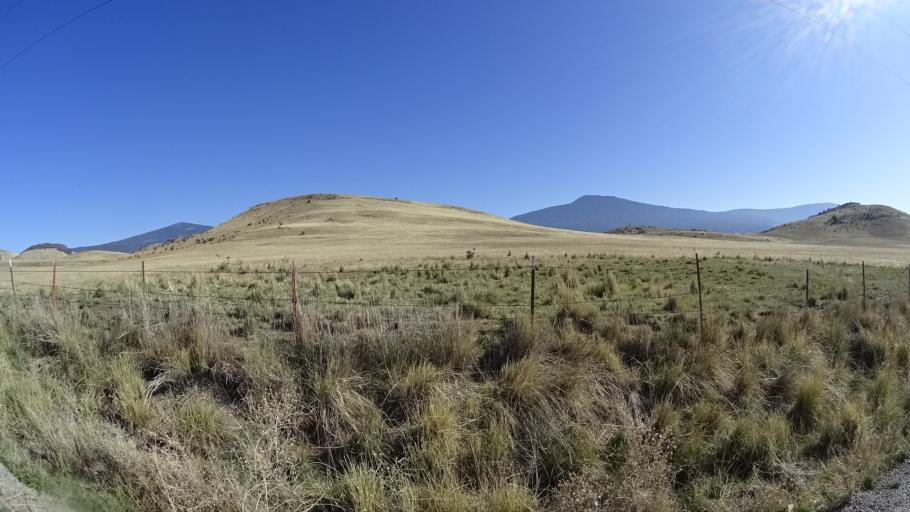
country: US
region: California
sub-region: Siskiyou County
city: Montague
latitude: 41.7568
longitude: -122.3593
